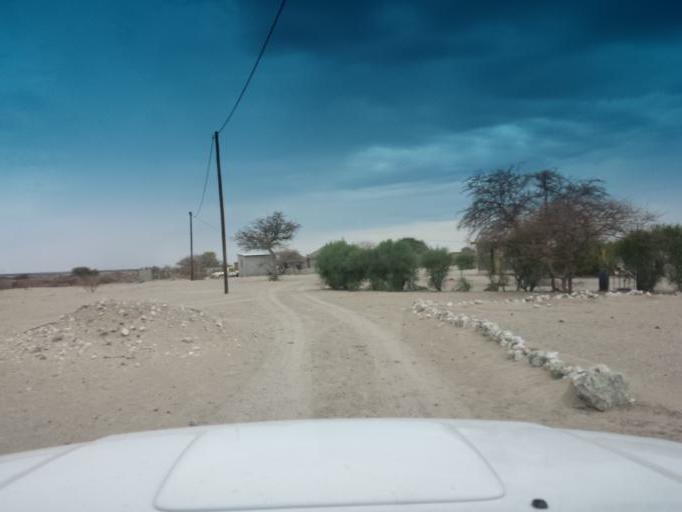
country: BW
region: Central
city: Mopipi
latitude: -21.1990
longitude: 24.8579
